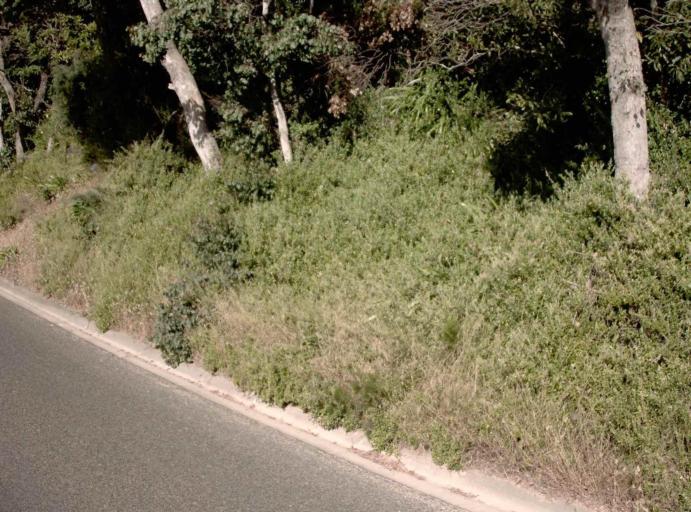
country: AU
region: Victoria
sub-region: East Gippsland
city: Lakes Entrance
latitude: -37.8897
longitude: 147.8559
